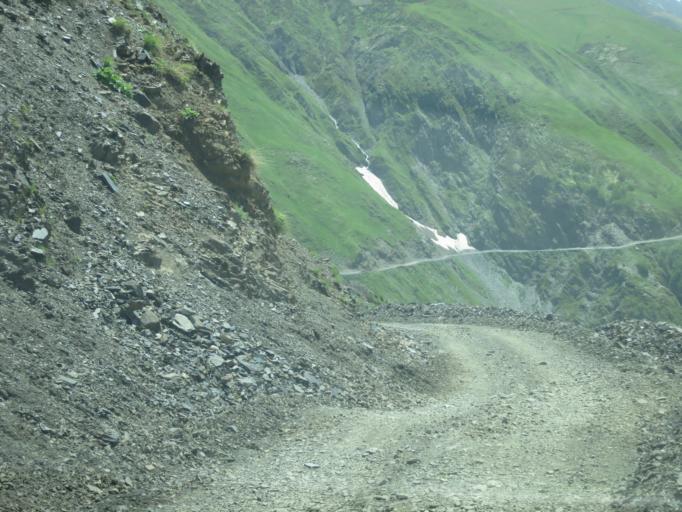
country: GE
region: Kakheti
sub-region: Telavi
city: Telavi
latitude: 42.2694
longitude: 45.4964
